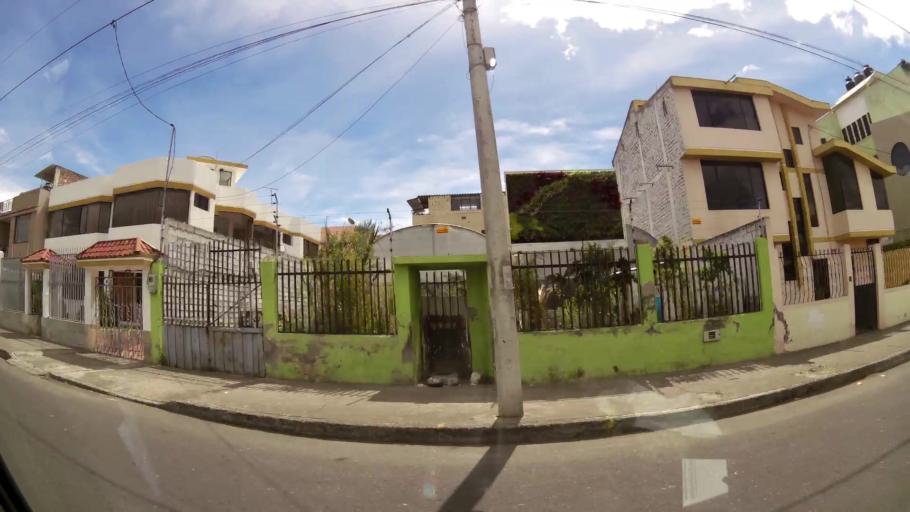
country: EC
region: Tungurahua
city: Ambato
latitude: -1.2621
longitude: -78.6240
